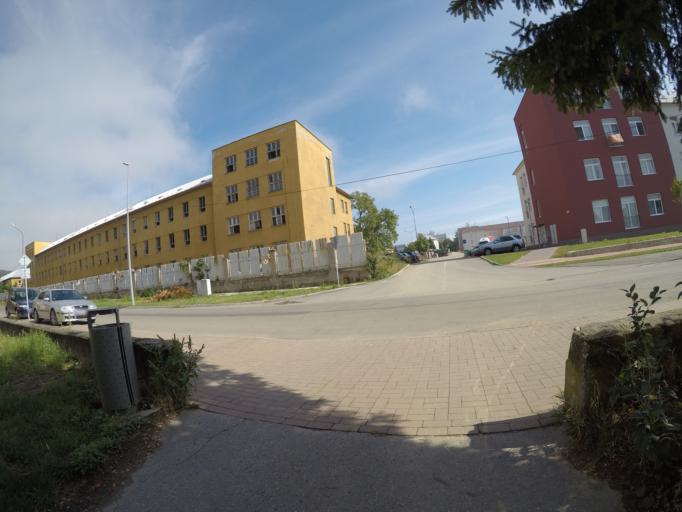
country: SK
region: Trenciansky
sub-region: Okres Nove Mesto nad Vahom
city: Nove Mesto nad Vahom
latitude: 48.7619
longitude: 17.8237
